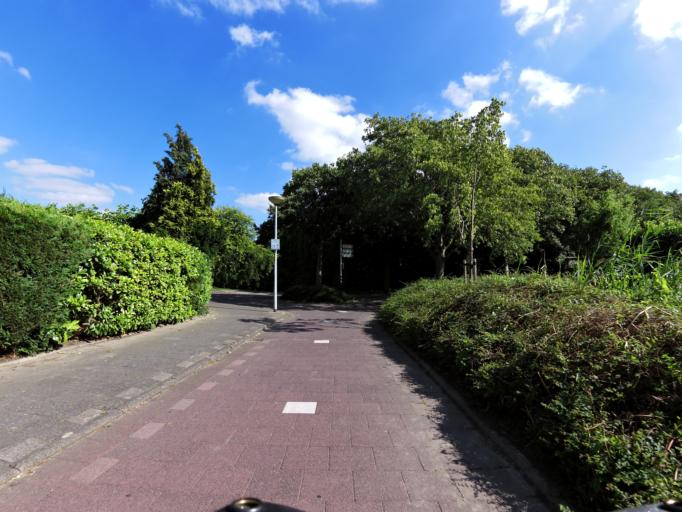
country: NL
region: South Holland
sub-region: Gemeente Barendrecht
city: Barendrecht
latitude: 51.8481
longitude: 4.5283
